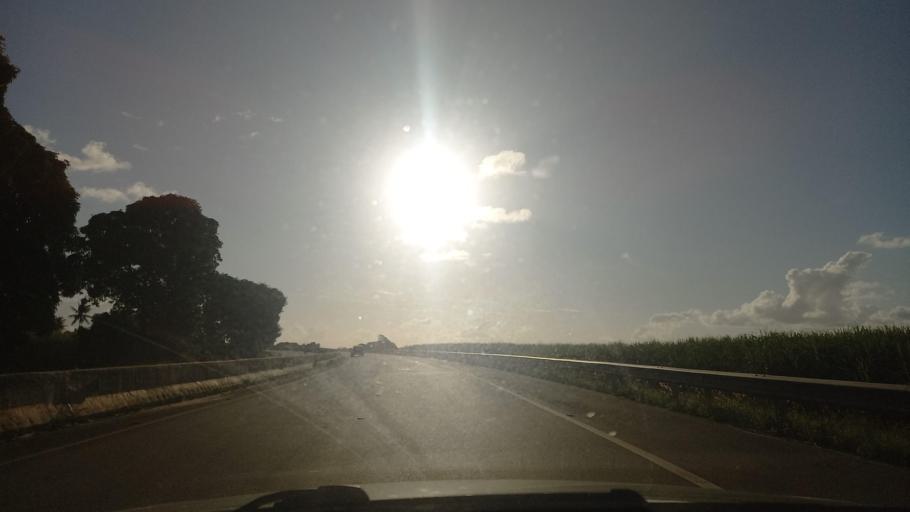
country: BR
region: Alagoas
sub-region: Campo Alegre
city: Campo Alegre
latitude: -9.8040
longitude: -36.2656
